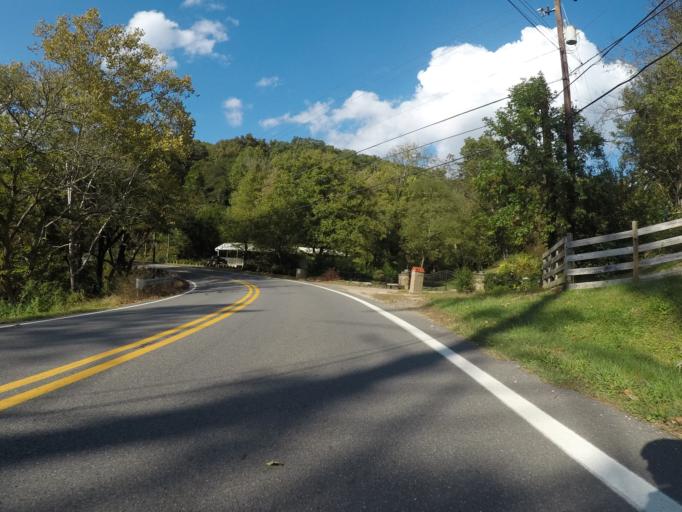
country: US
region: Ohio
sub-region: Lawrence County
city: Burlington
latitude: 38.3608
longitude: -82.5053
